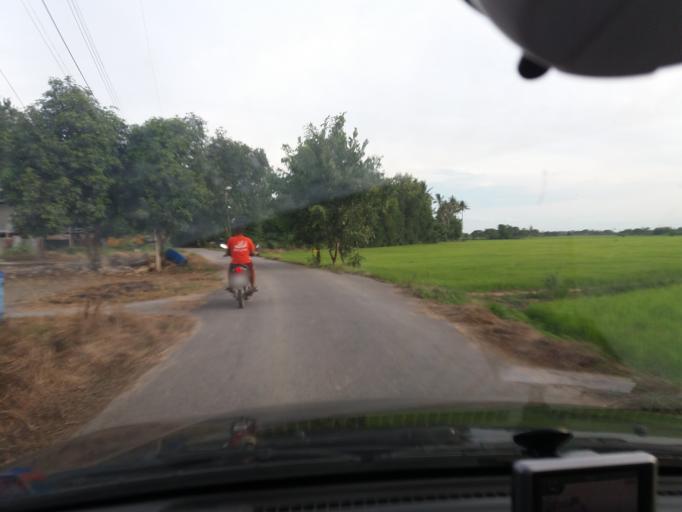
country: TH
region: Suphan Buri
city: Doembang Nangbuat
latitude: 14.8159
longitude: 100.1384
